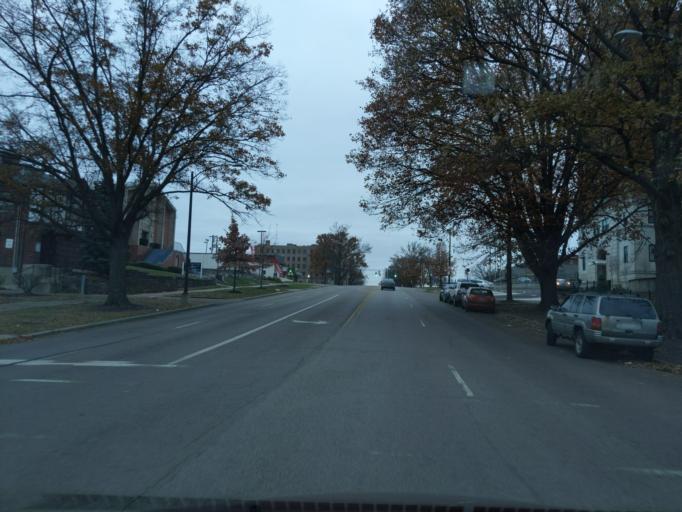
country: US
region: Kentucky
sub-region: Campbell County
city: Dayton
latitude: 39.1271
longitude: -84.4843
